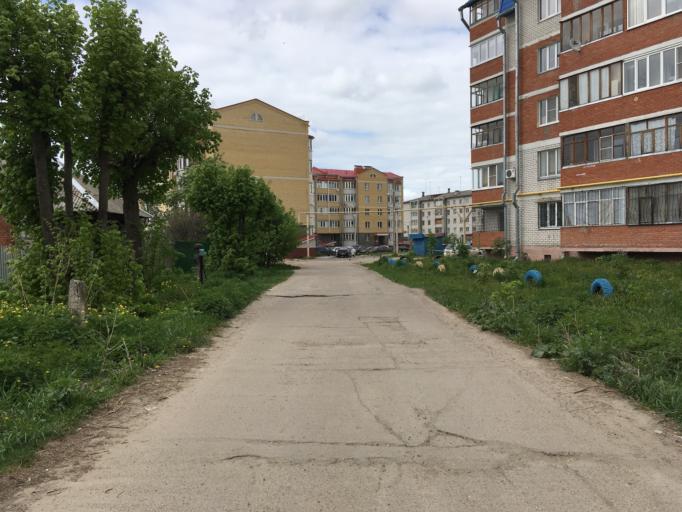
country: RU
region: Mariy-El
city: Yoshkar-Ola
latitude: 56.6475
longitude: 47.8596
